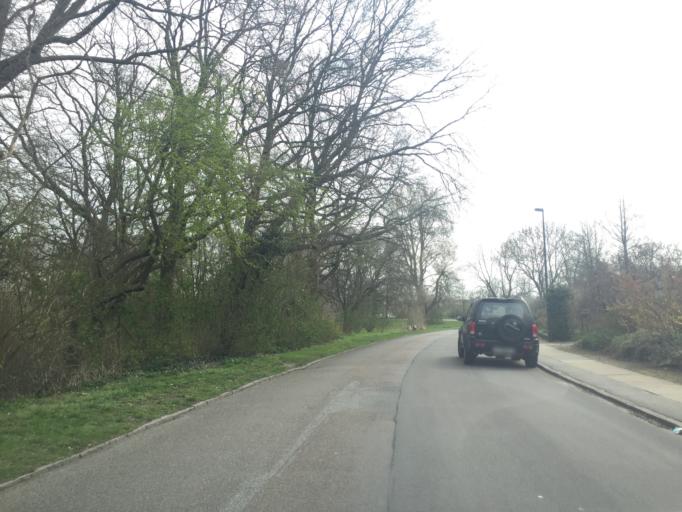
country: DK
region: Capital Region
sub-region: Kobenhavn
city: Vanlose
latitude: 55.7123
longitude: 12.4974
